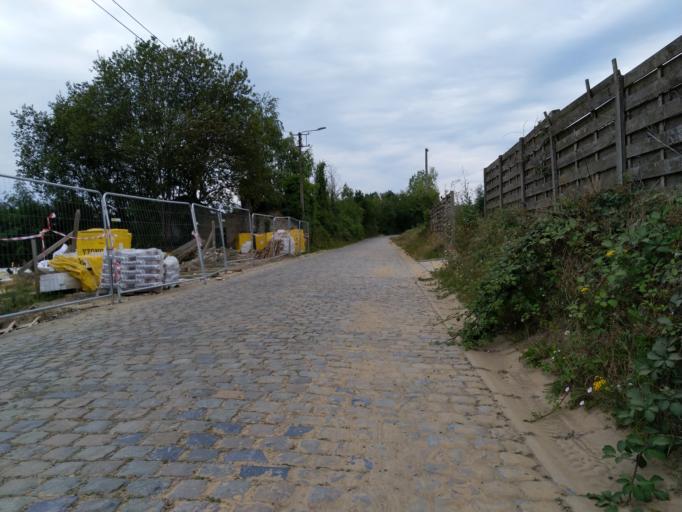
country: BE
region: Wallonia
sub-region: Province du Hainaut
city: Mons
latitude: 50.4923
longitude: 4.0124
